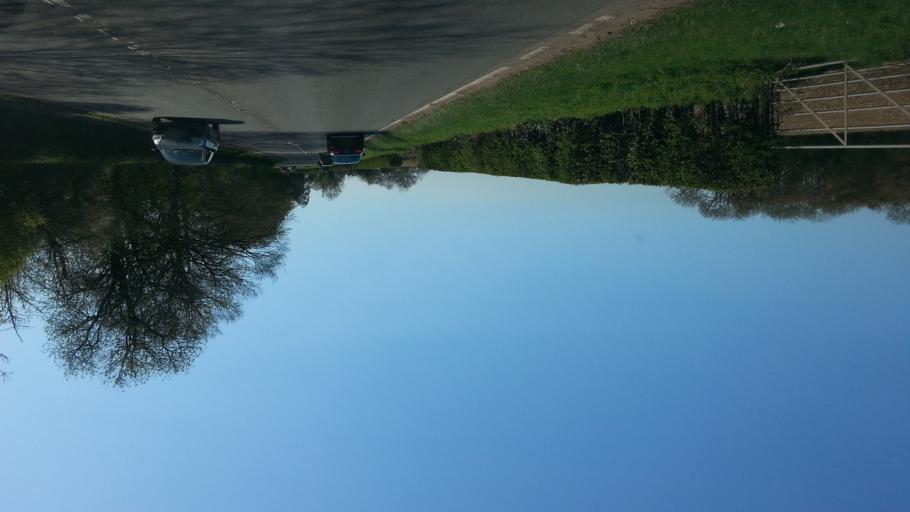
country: GB
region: England
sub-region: Worcestershire
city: Alvechurch
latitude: 52.3855
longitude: -1.9580
